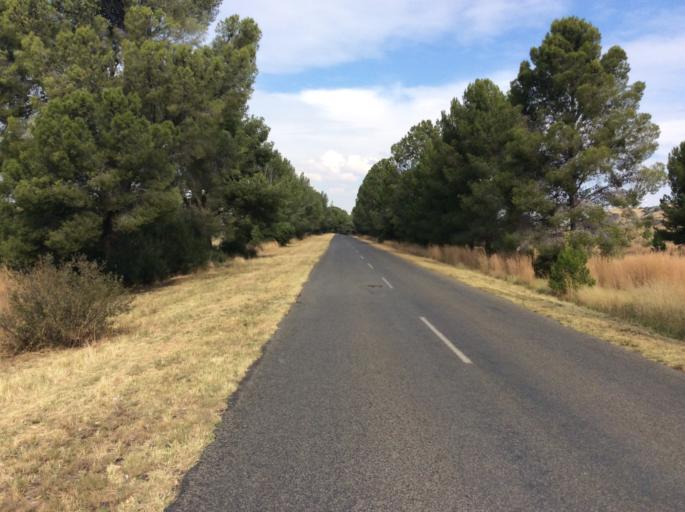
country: ZA
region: Orange Free State
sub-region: Xhariep District Municipality
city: Dewetsdorp
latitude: -29.5687
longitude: 26.6658
